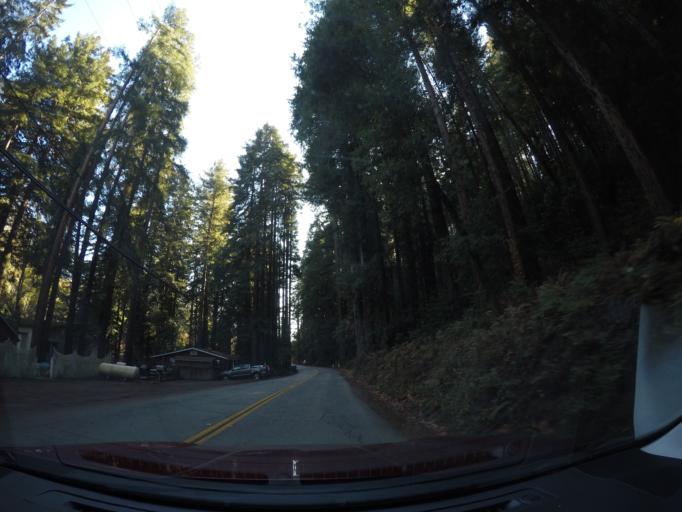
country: US
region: California
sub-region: Santa Cruz County
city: Scotts Valley
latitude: 37.0620
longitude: -122.0348
